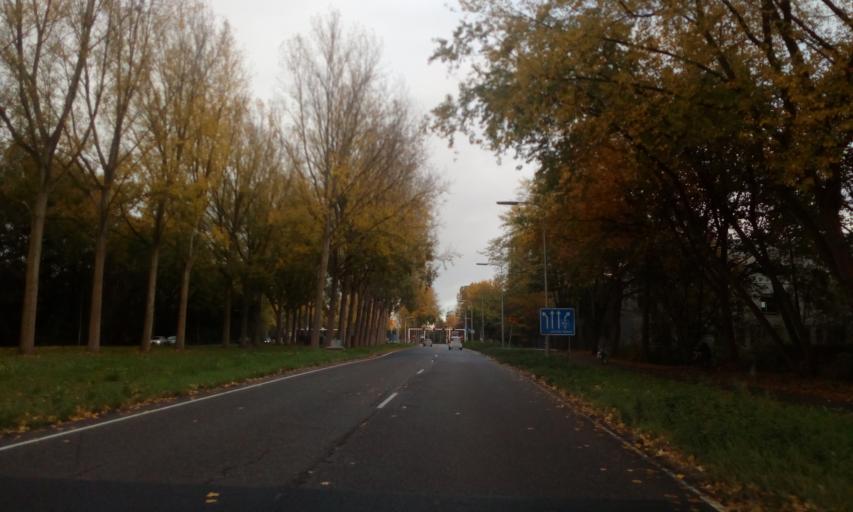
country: NL
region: South Holland
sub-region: Gemeente Delft
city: Delft
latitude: 51.9980
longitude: 4.3488
